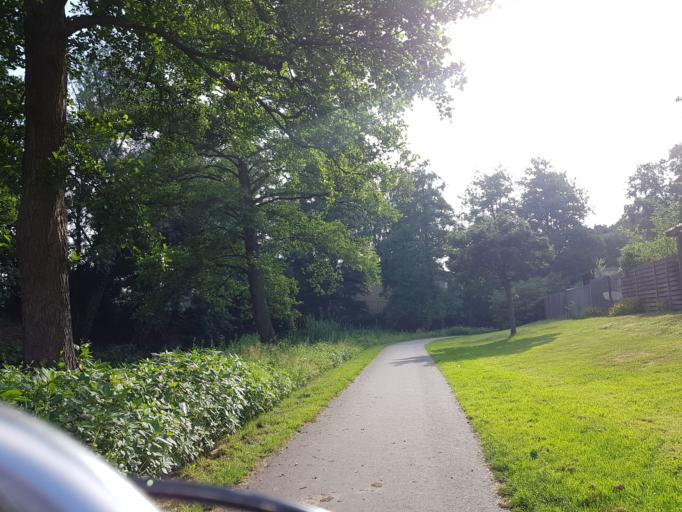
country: NL
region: Gelderland
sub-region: Gemeente Apeldoorn
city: Apeldoorn
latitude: 52.1890
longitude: 5.9921
